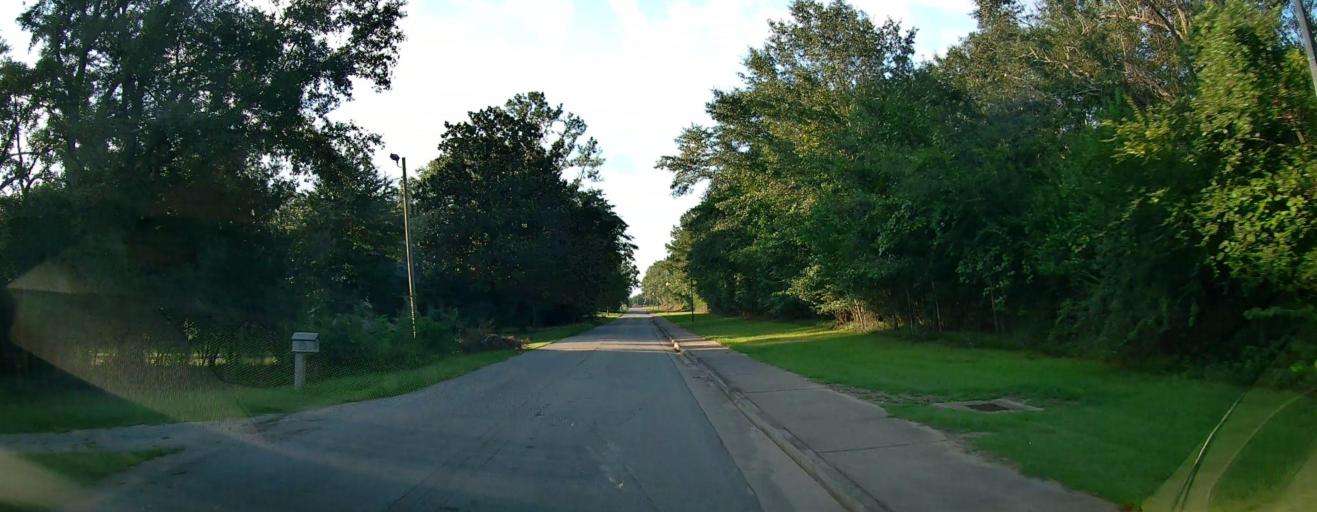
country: US
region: Georgia
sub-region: Crawford County
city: Roberta
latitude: 32.7133
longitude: -84.0092
